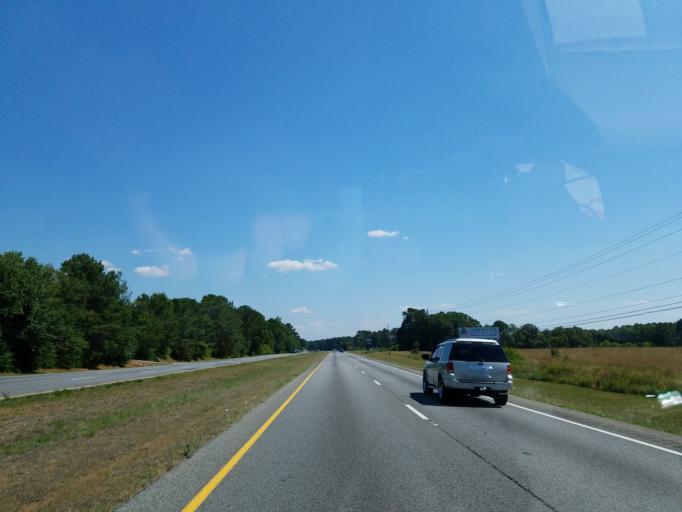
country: US
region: Georgia
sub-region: Clayton County
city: Lovejoy
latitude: 33.4370
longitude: -84.3208
